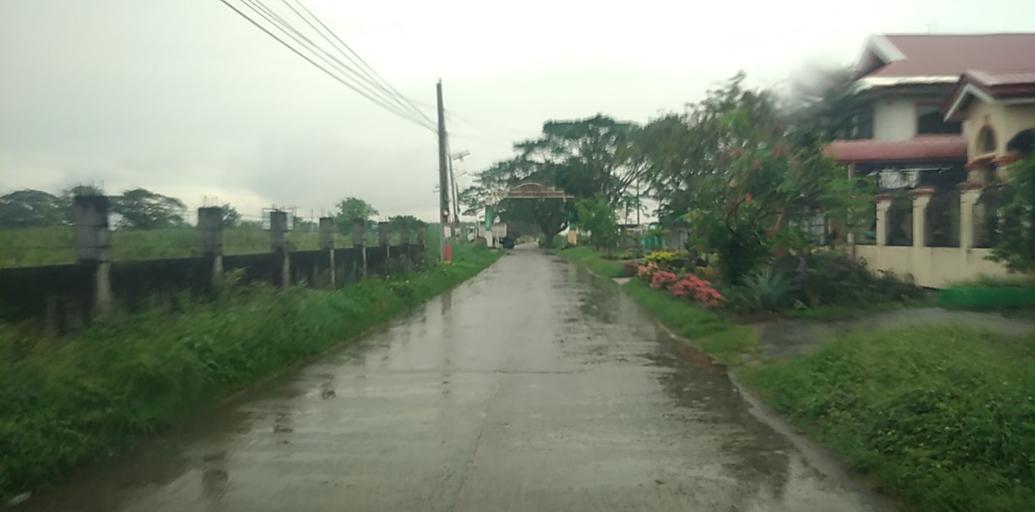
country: PH
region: Central Luzon
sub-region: Province of Pampanga
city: San Antonio
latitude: 15.1598
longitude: 120.6935
